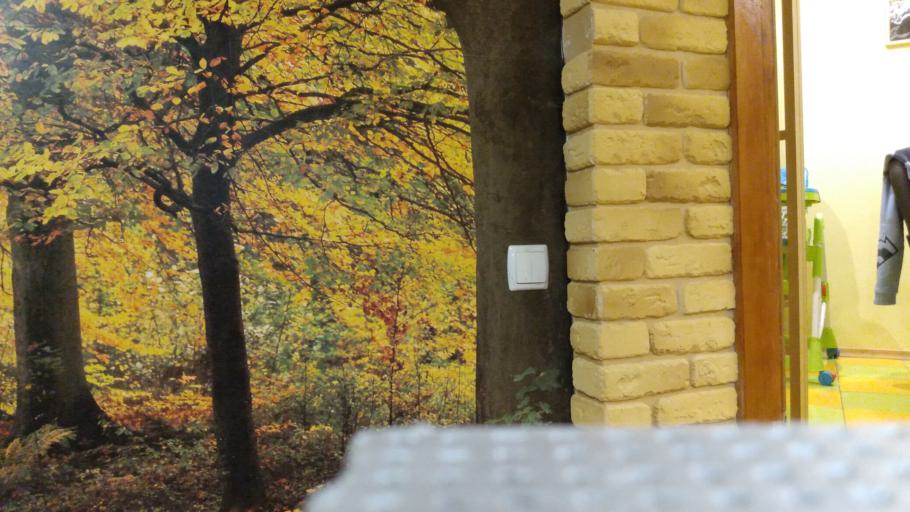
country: RU
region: Vologda
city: Babayevo
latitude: 59.3644
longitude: 35.9997
